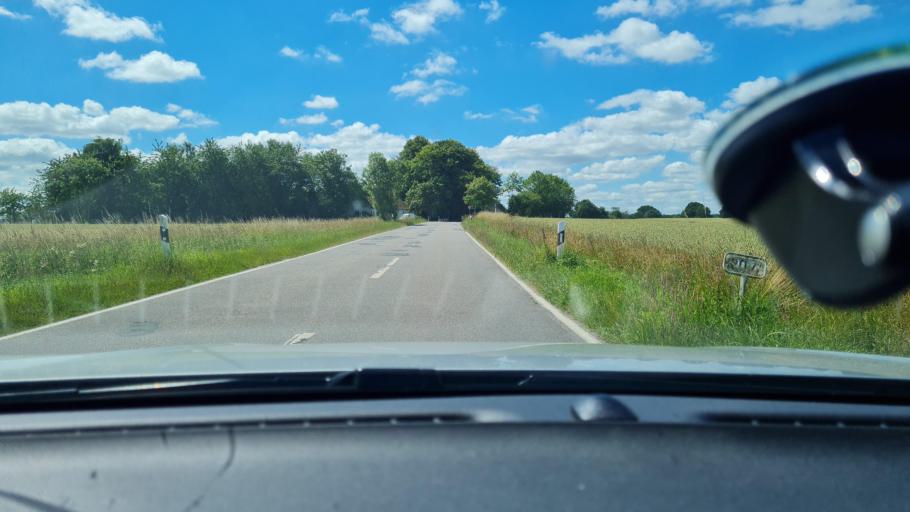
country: DE
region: Schleswig-Holstein
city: Thumby
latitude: 54.5991
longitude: 9.9148
